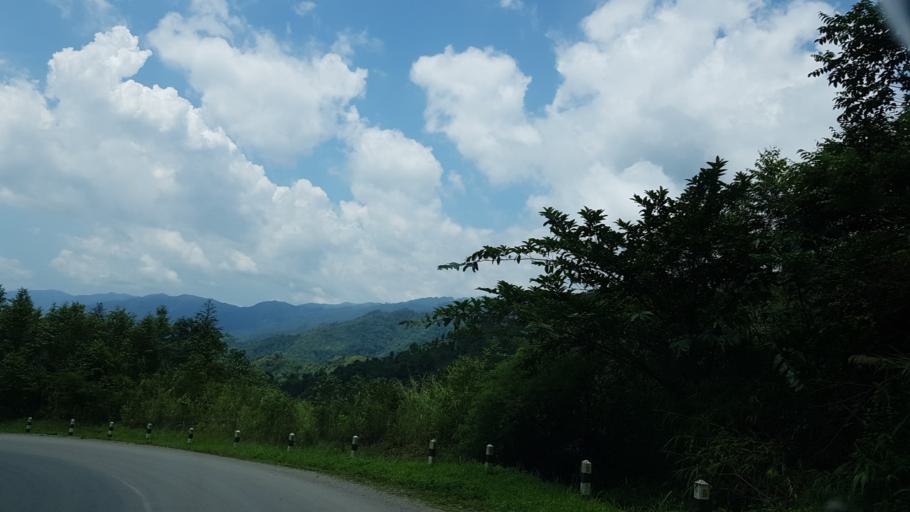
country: LA
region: Vientiane
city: Muang Kasi
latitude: 19.3769
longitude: 102.1568
